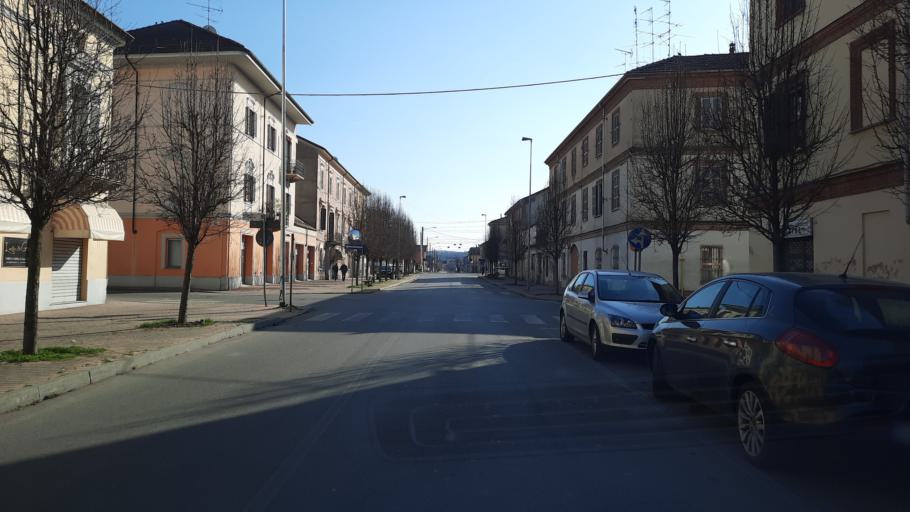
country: IT
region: Piedmont
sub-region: Provincia di Vercelli
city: Trino
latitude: 45.1908
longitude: 8.2962
